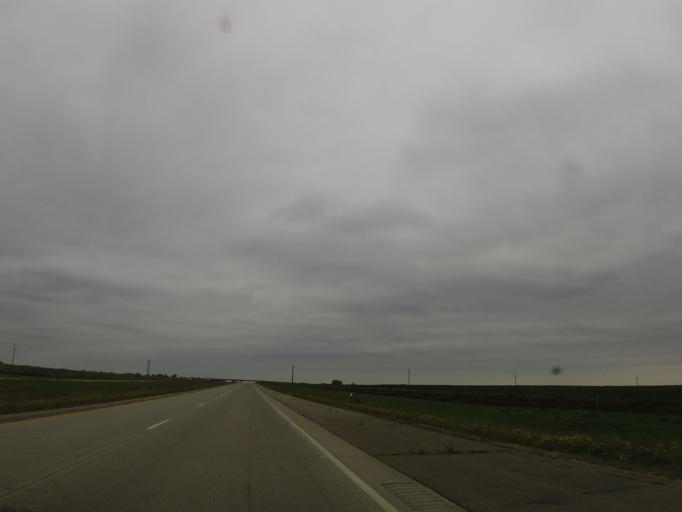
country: US
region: South Dakota
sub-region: Roberts County
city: Sisseton
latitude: 45.4463
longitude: -96.9892
